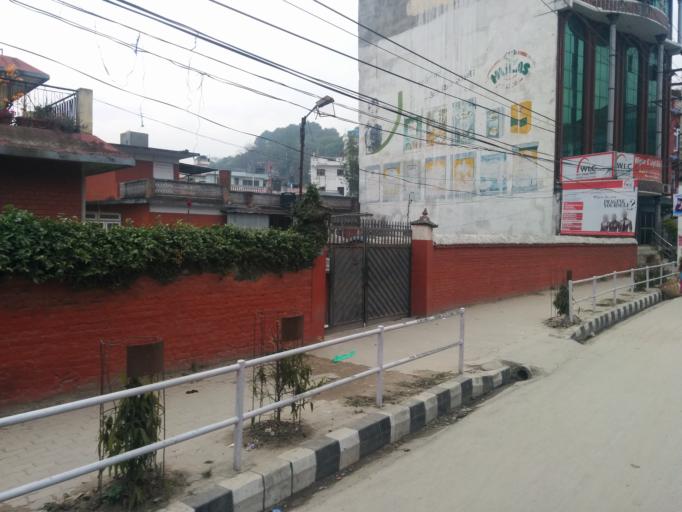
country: NP
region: Central Region
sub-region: Bagmati Zone
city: Kathmandu
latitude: 27.7081
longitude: 85.3388
